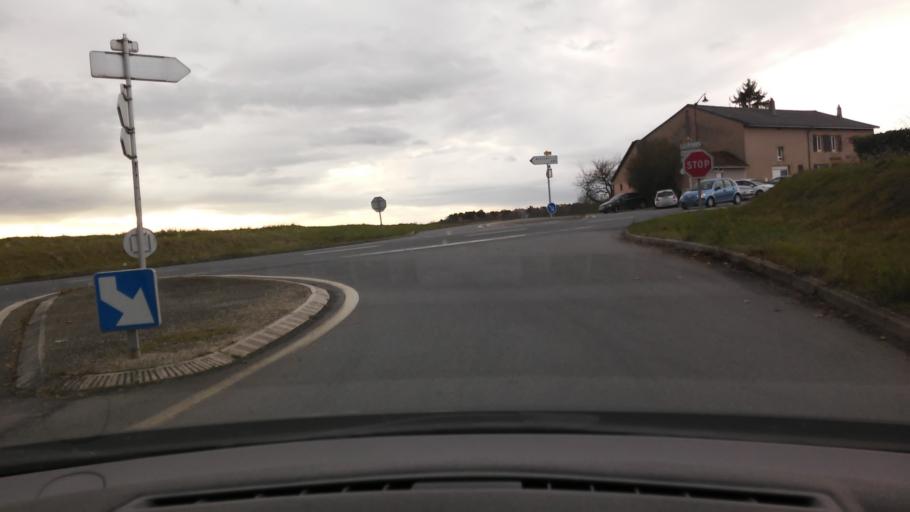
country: FR
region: Lorraine
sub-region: Departement de la Moselle
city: Saint-Julien-les-Metz
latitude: 49.1491
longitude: 6.2472
